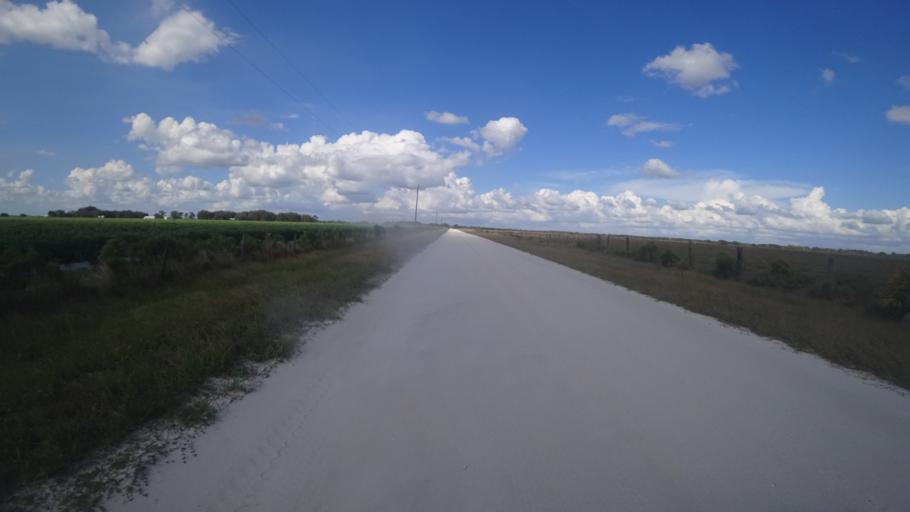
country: US
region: Florida
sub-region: DeSoto County
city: Arcadia
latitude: 27.3045
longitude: -82.0806
